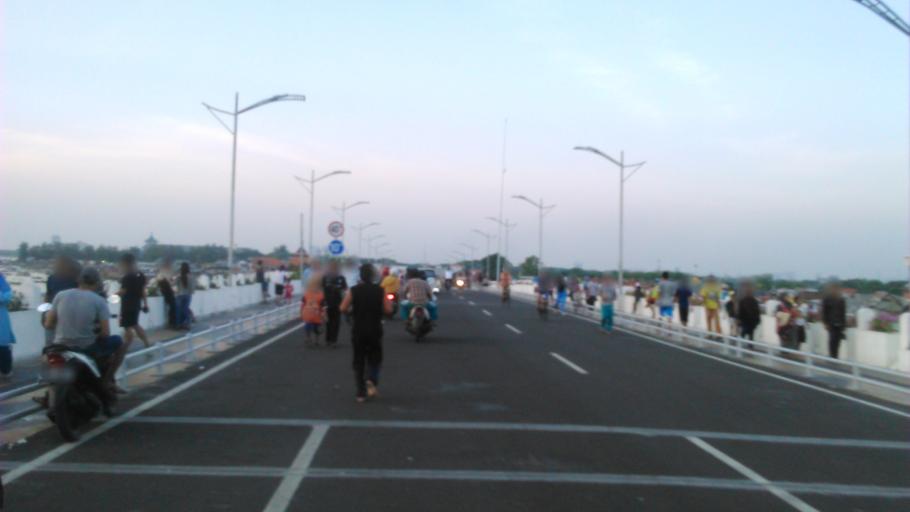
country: ID
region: East Java
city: Labansari
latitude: -7.2376
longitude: 112.7971
